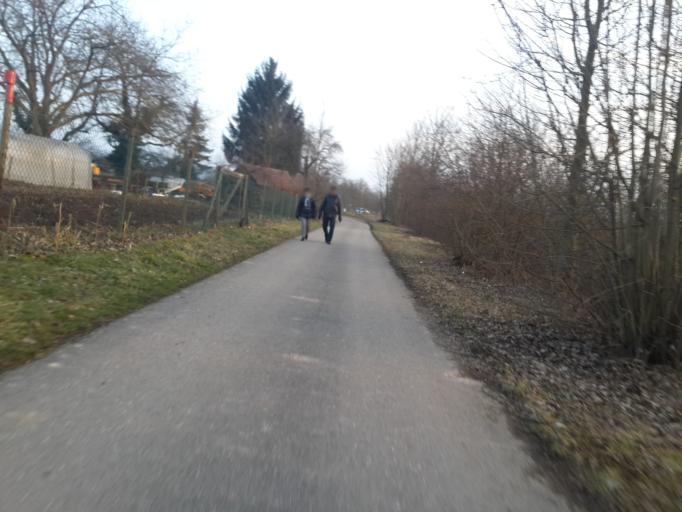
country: DE
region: Baden-Wuerttemberg
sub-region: Regierungsbezirk Stuttgart
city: Flein
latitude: 49.1124
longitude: 9.1839
